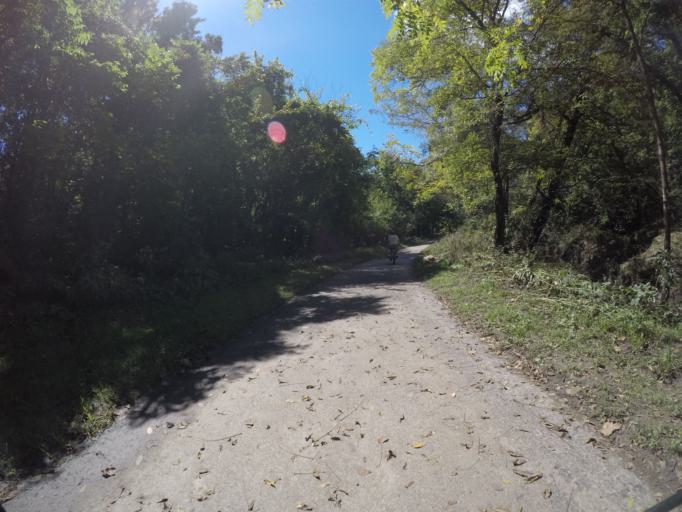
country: US
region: Kansas
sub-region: Johnson County
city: Lenexa
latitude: 38.8997
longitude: -94.7489
